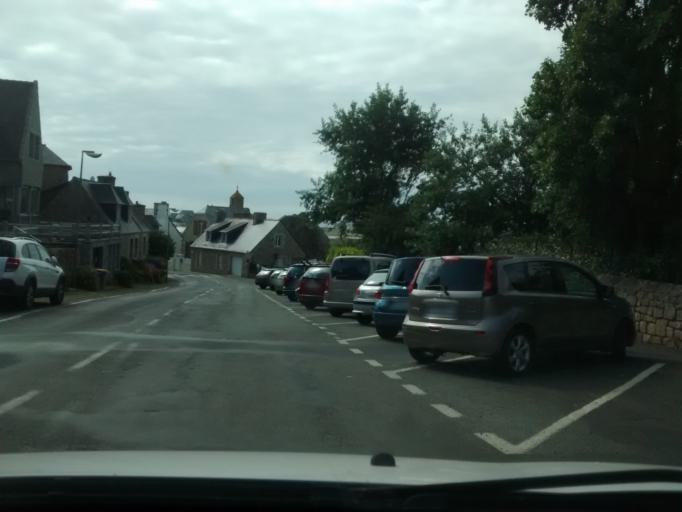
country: FR
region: Brittany
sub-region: Departement des Cotes-d'Armor
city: Penvenan
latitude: 48.8363
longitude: -3.3108
